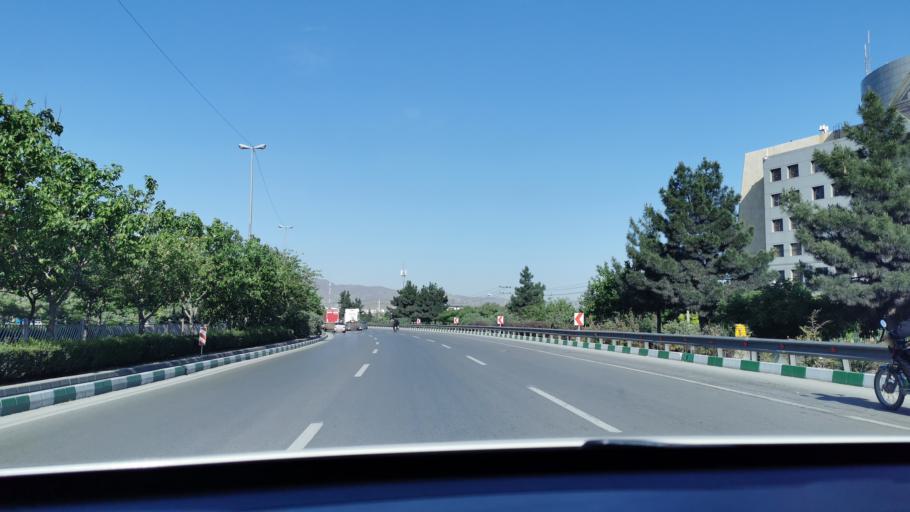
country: IR
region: Razavi Khorasan
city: Mashhad
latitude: 36.2582
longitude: 59.6258
